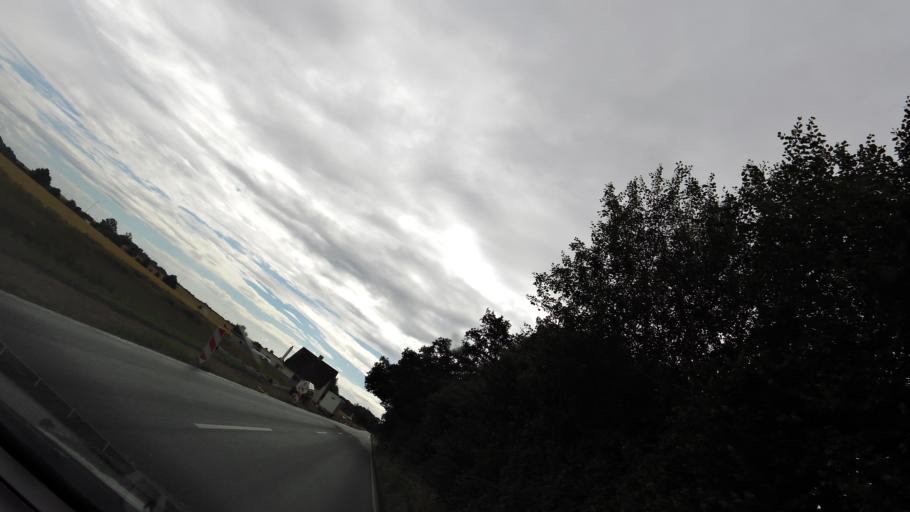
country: DK
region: South Denmark
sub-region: Nordfyns Kommune
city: Sonderso
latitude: 55.4779
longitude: 10.2261
